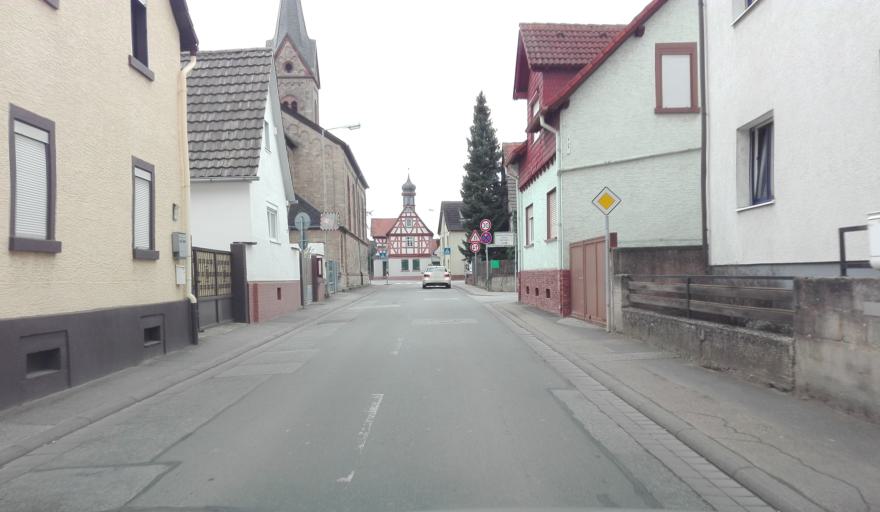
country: DE
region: Hesse
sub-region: Regierungsbezirk Darmstadt
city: Einhausen
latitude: 49.7043
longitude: 8.5707
